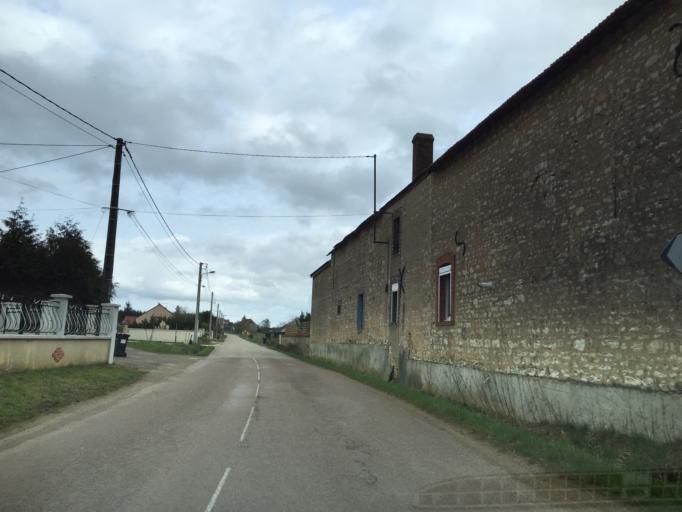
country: FR
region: Bourgogne
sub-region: Departement de l'Yonne
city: Charbuy
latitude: 47.8001
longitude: 3.4369
